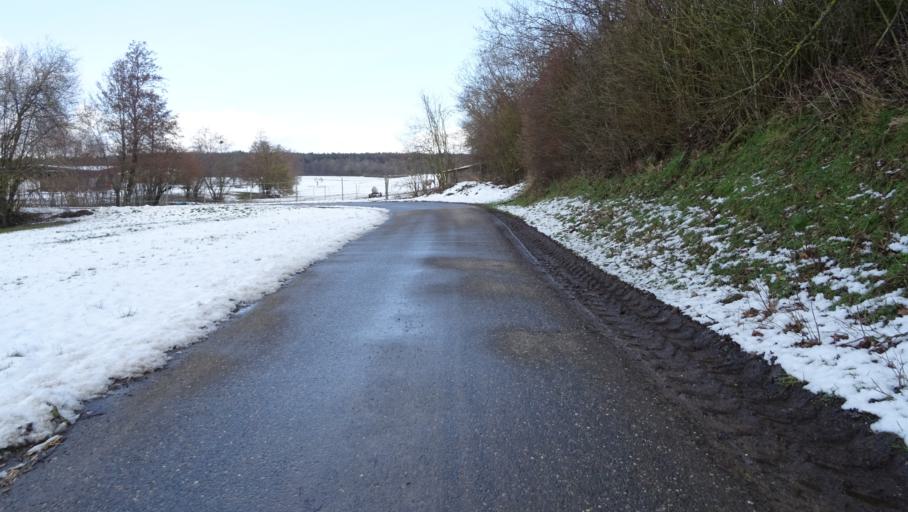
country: DE
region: Baden-Wuerttemberg
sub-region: Karlsruhe Region
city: Limbach
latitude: 49.4285
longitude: 9.2684
